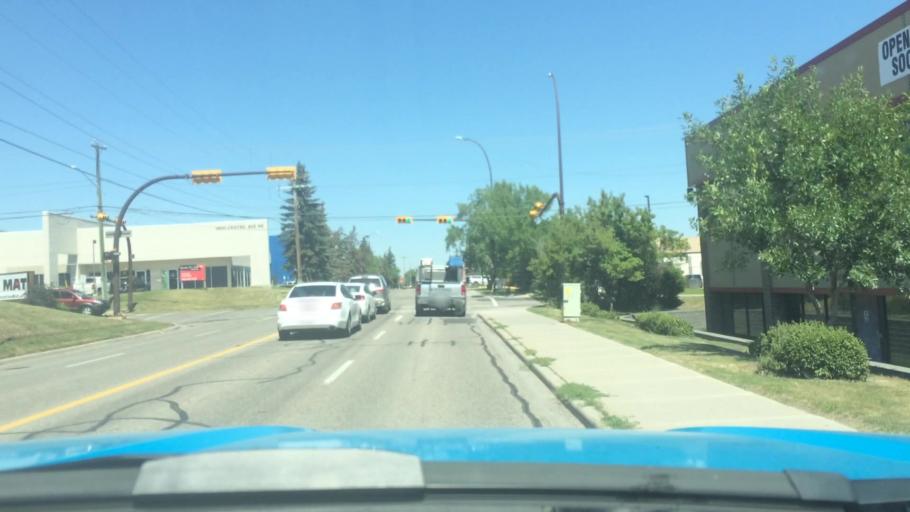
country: CA
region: Alberta
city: Calgary
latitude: 51.0519
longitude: -113.9932
